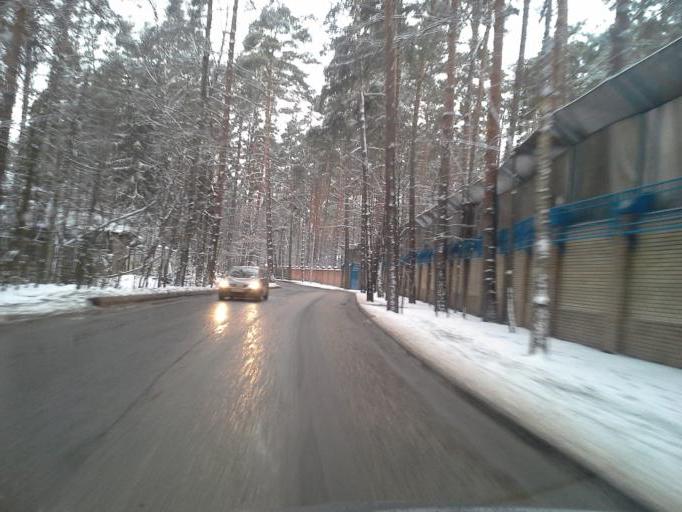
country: RU
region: Moskovskaya
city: Nikolina Gora
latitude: 55.7364
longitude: 37.0404
